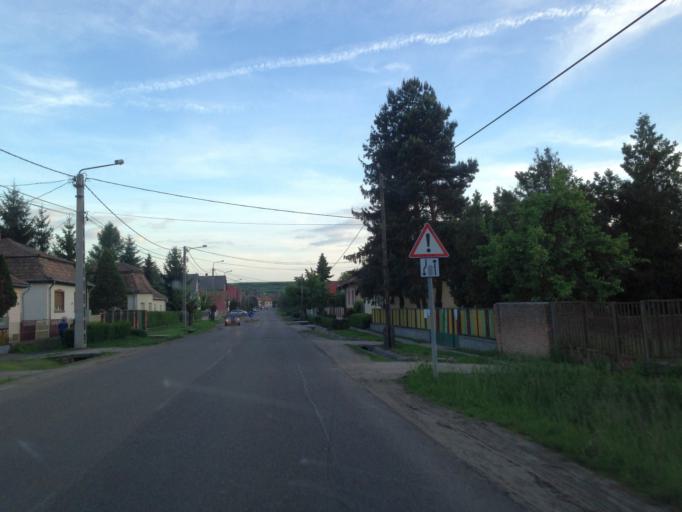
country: HU
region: Nograd
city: Tar
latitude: 47.9546
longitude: 19.7460
